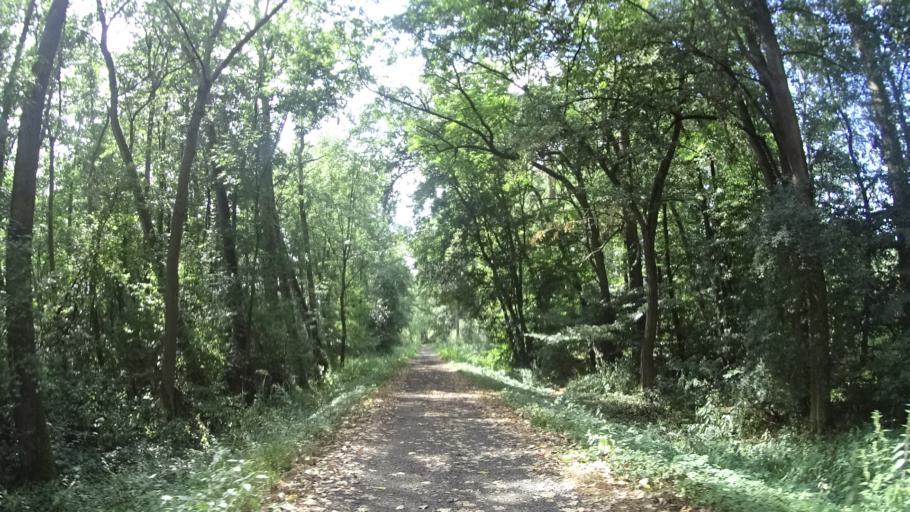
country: CZ
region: Olomoucky
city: Skrben
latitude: 49.6742
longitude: 17.1692
